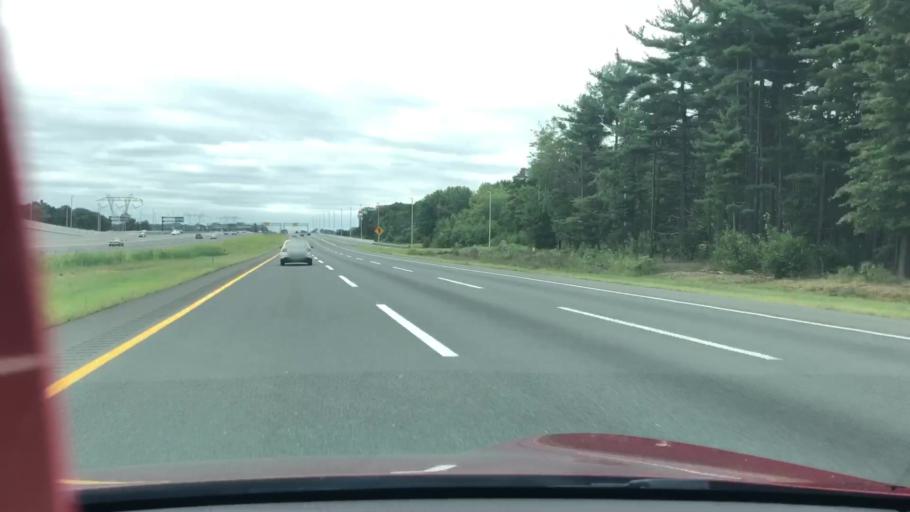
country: US
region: New Jersey
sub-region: Burlington County
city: Bordentown
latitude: 40.0931
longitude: -74.7303
